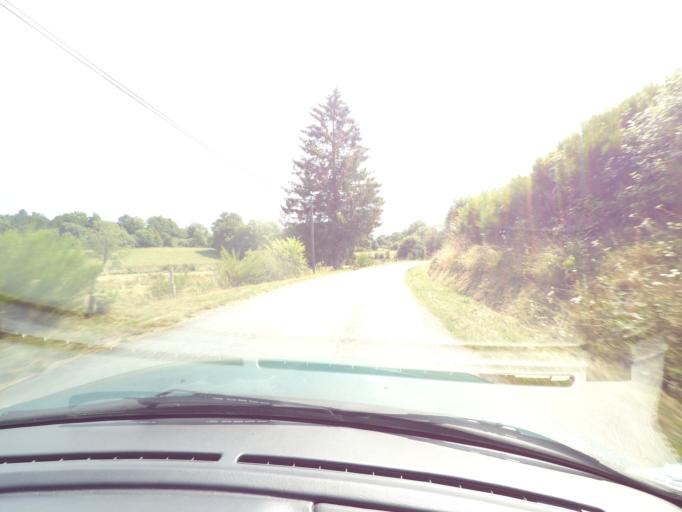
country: FR
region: Limousin
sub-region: Departement de la Correze
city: Bugeat
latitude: 45.7479
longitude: 1.9607
